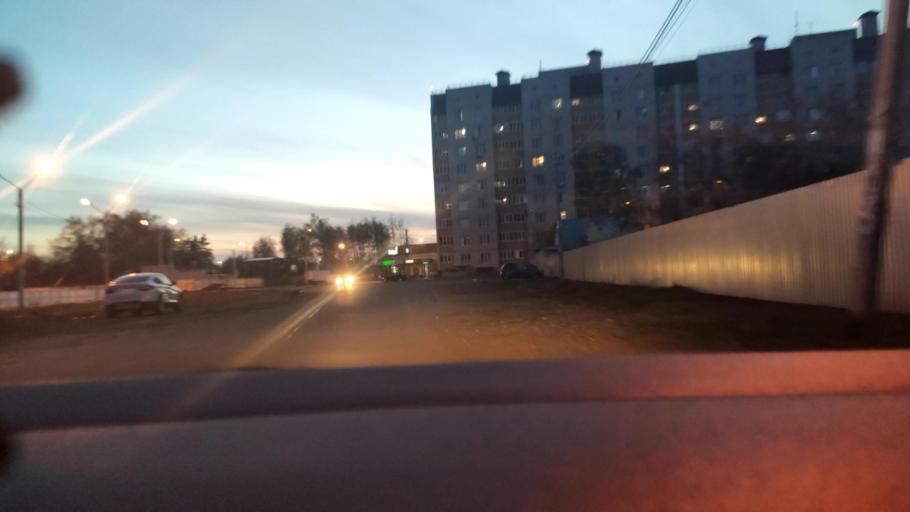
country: RU
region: Voronezj
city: Somovo
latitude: 51.7367
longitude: 39.3190
